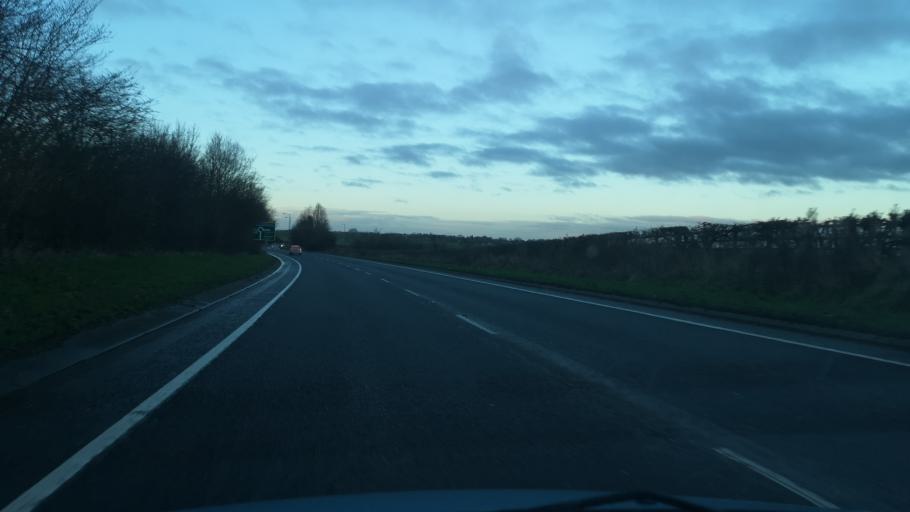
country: GB
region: England
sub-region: City and Borough of Wakefield
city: Hemsworth
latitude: 53.6256
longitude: -1.3360
